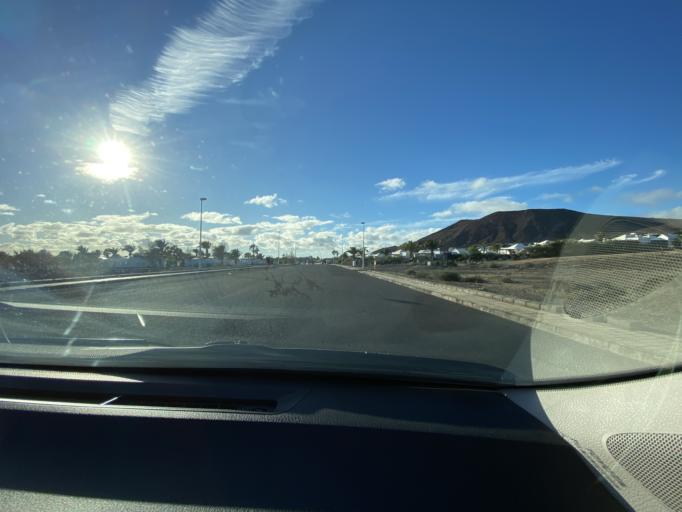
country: ES
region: Canary Islands
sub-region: Provincia de Las Palmas
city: Playa Blanca
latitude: 28.8639
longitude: -13.8456
